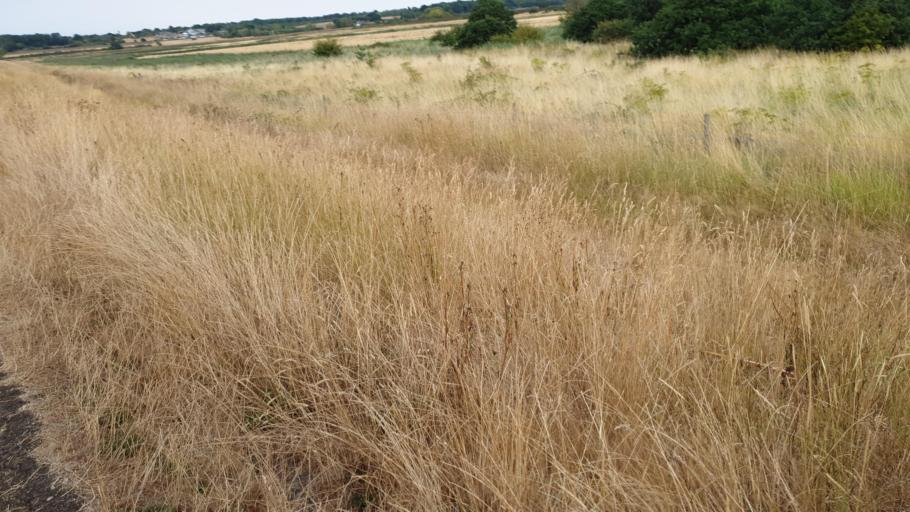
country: GB
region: England
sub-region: Essex
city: Alresford
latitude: 51.8301
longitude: 0.9859
